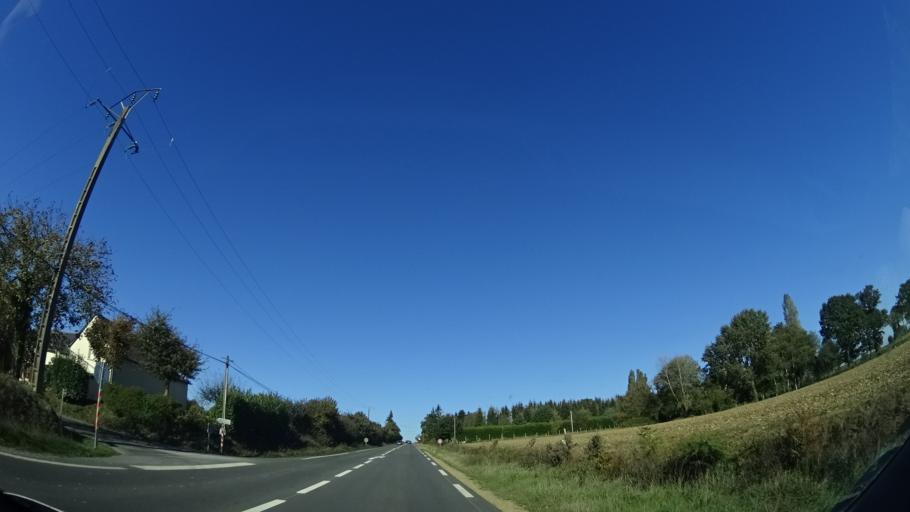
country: FR
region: Brittany
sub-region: Departement d'Ille-et-Vilaine
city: Melesse
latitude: 48.1912
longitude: -1.6927
